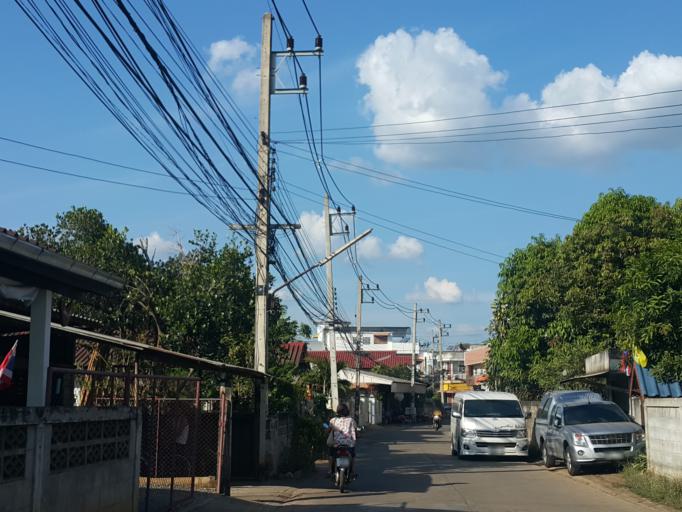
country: TH
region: Sukhothai
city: Thung Saliam
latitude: 17.3159
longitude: 99.5530
